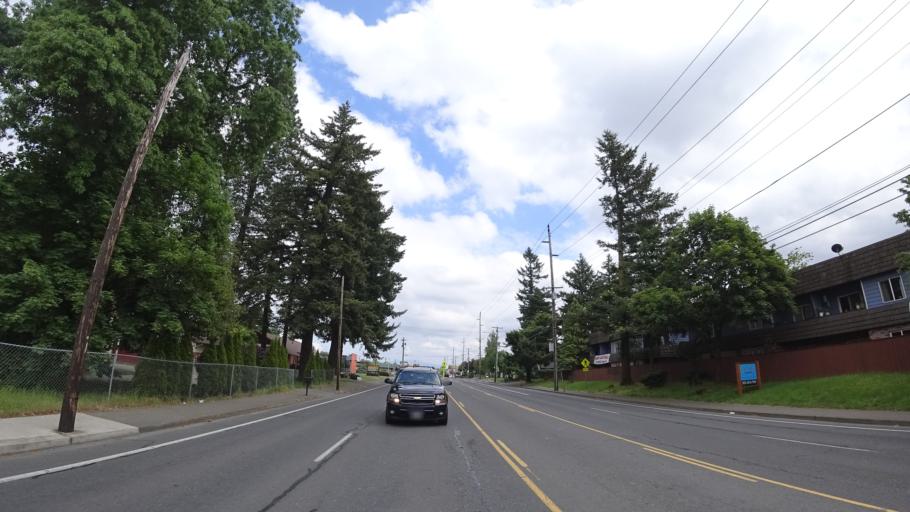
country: US
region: Oregon
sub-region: Multnomah County
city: Fairview
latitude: 45.5192
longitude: -122.4806
